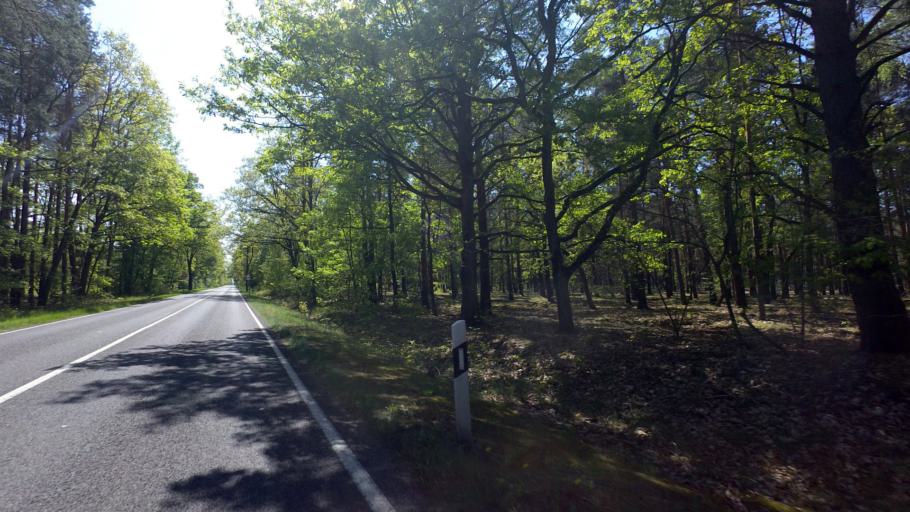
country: DE
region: Brandenburg
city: Bestensee
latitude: 52.2194
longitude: 13.6855
